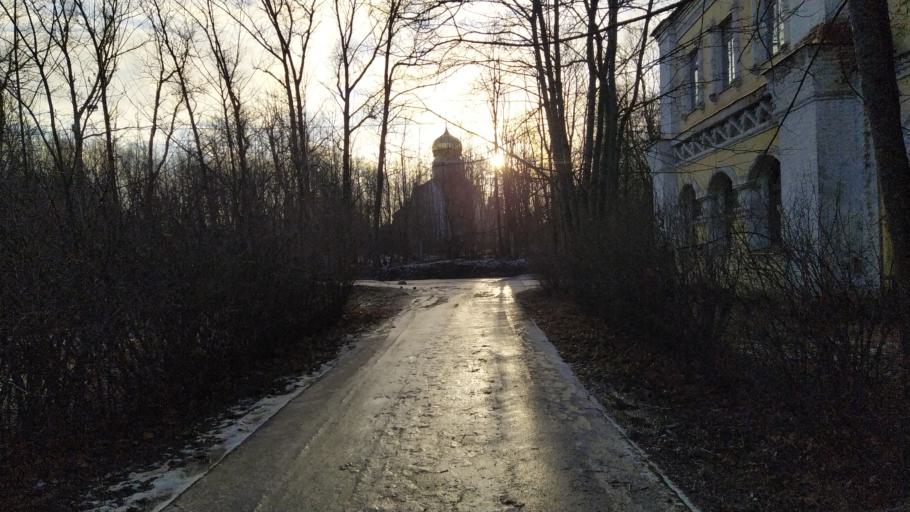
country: RU
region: St.-Petersburg
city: Pushkin
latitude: 59.7274
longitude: 30.3924
